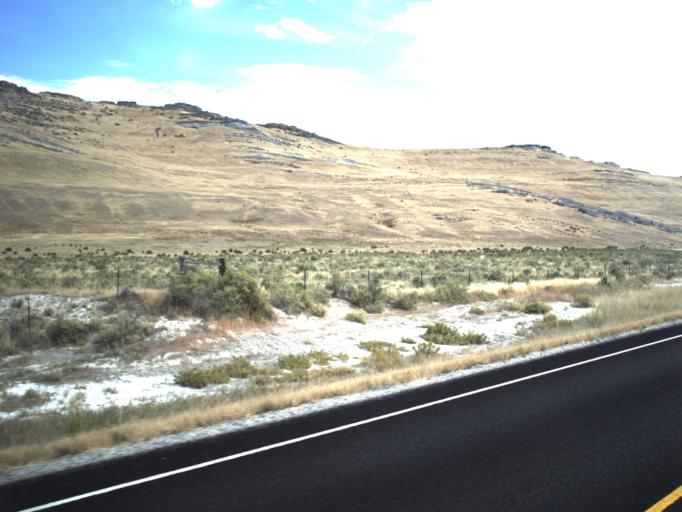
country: US
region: Utah
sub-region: Box Elder County
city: Tremonton
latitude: 41.6225
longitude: -112.3898
